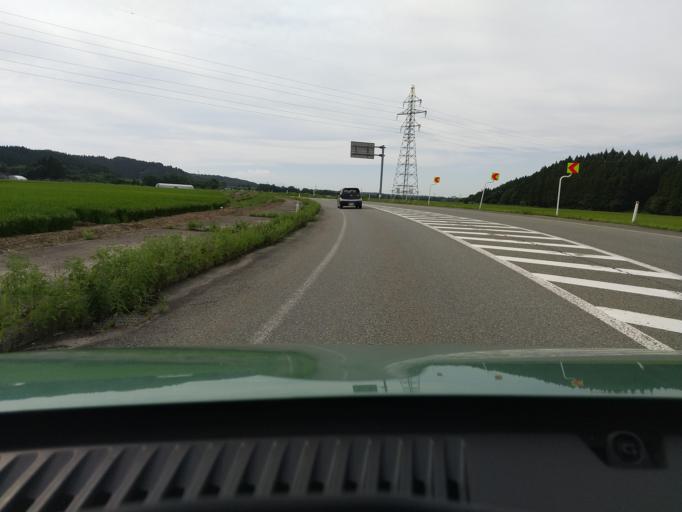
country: JP
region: Akita
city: Akita Shi
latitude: 39.7918
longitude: 140.1112
